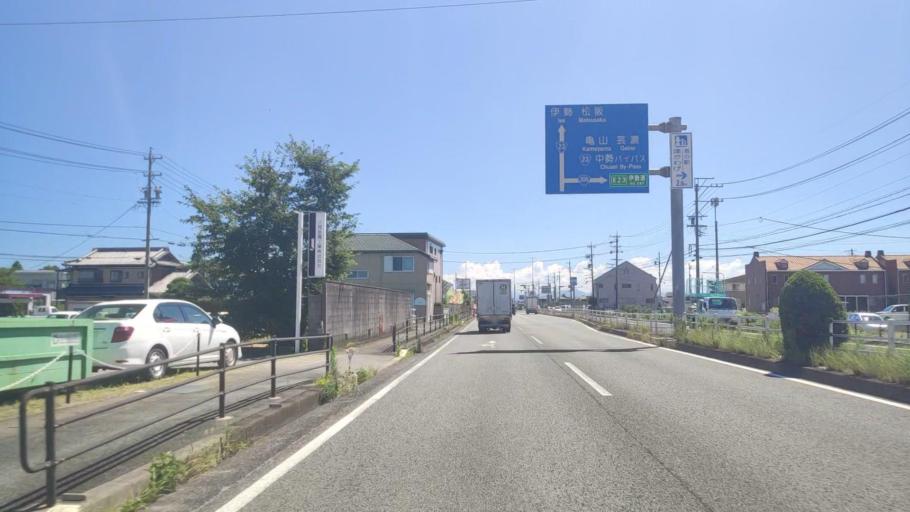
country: JP
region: Mie
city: Kawage
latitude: 34.7777
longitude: 136.5314
